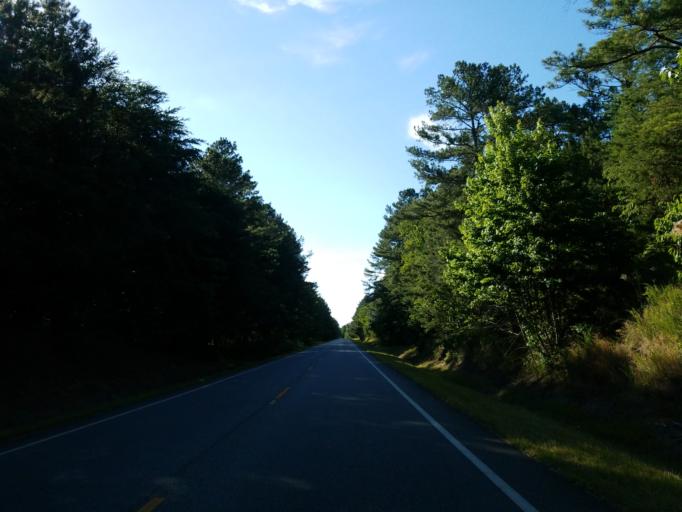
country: US
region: Georgia
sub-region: Gordon County
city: Calhoun
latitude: 34.5828
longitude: -85.0011
